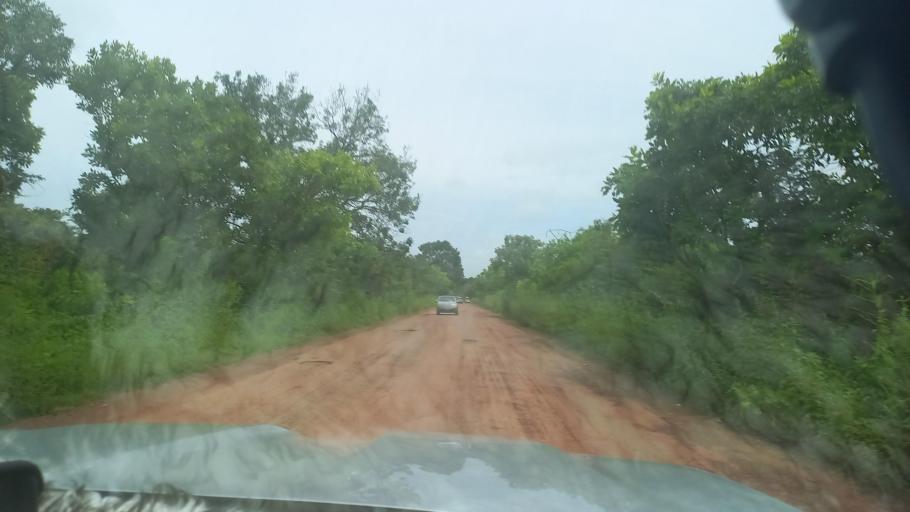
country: SN
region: Kolda
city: Marsassoum
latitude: 12.9036
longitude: -16.0211
